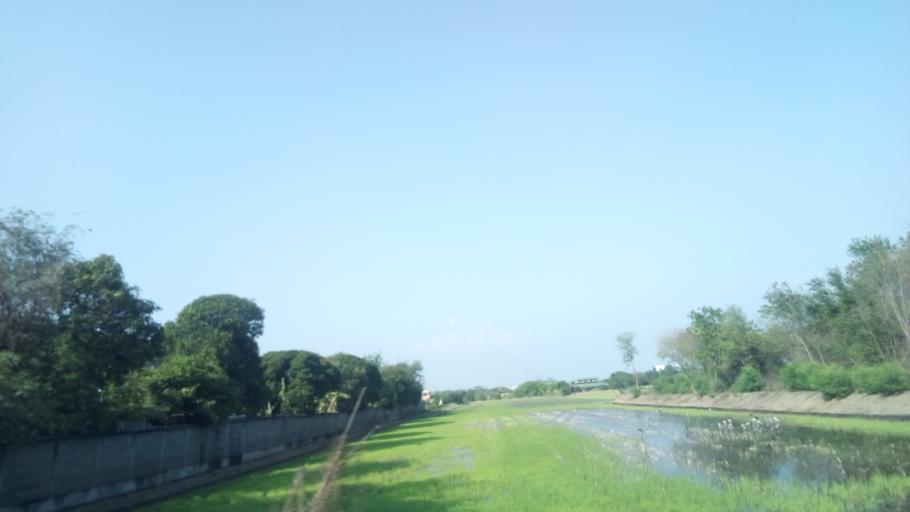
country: TH
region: Nonthaburi
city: Bang Bua Thong
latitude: 13.9347
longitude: 100.3709
